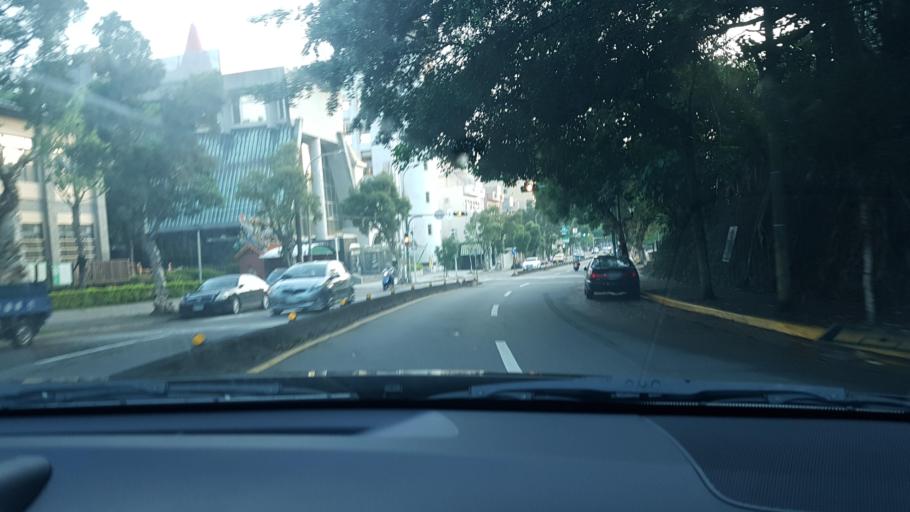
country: TW
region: Taipei
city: Taipei
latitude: 25.1017
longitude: 121.5523
